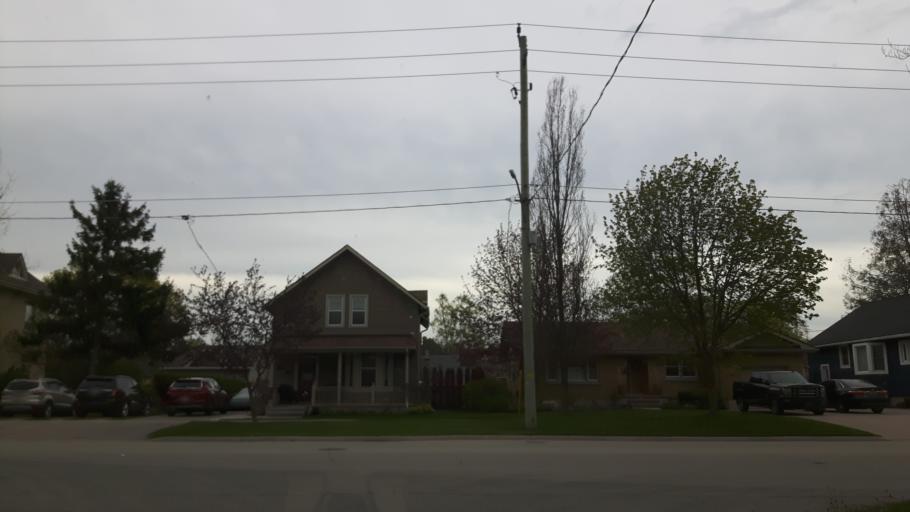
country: CA
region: Ontario
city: Goderich
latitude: 43.7407
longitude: -81.7126
